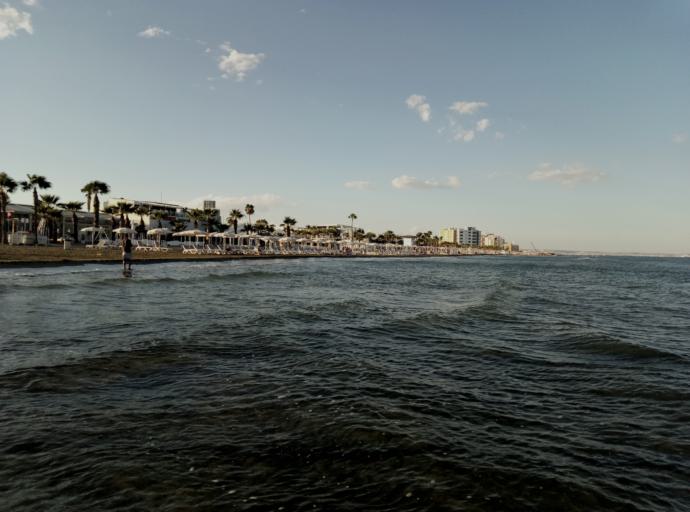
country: CY
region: Larnaka
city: Larnaca
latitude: 34.8868
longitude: 33.6373
